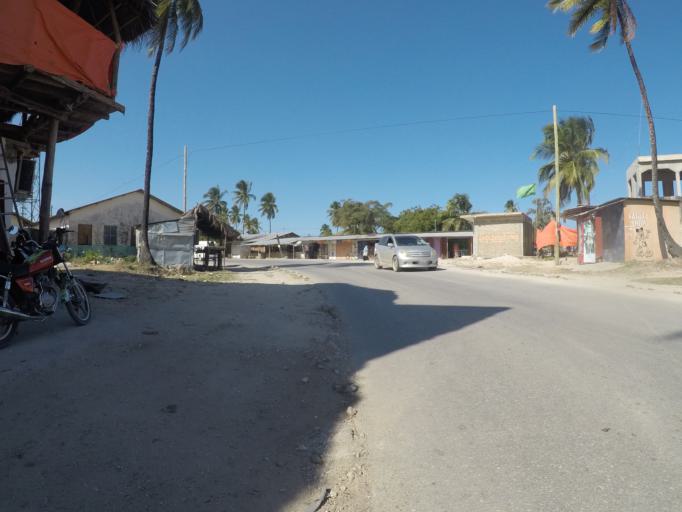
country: TZ
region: Zanzibar Central/South
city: Nganane
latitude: -6.2650
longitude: 39.5325
